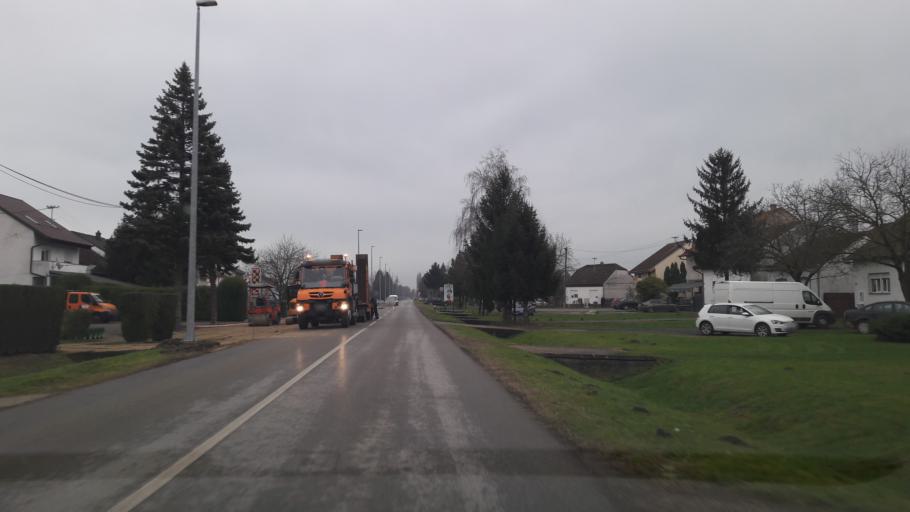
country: HR
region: Osjecko-Baranjska
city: Josipovac
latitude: 45.5878
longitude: 18.5756
